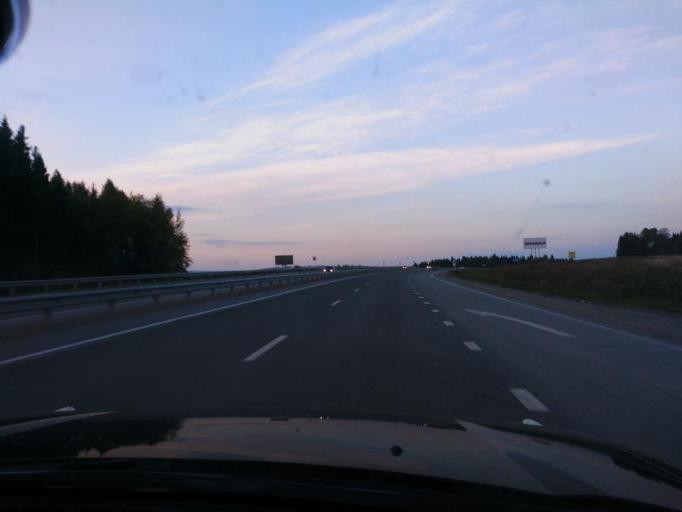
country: RU
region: Perm
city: Polazna
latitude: 58.2711
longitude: 56.4151
